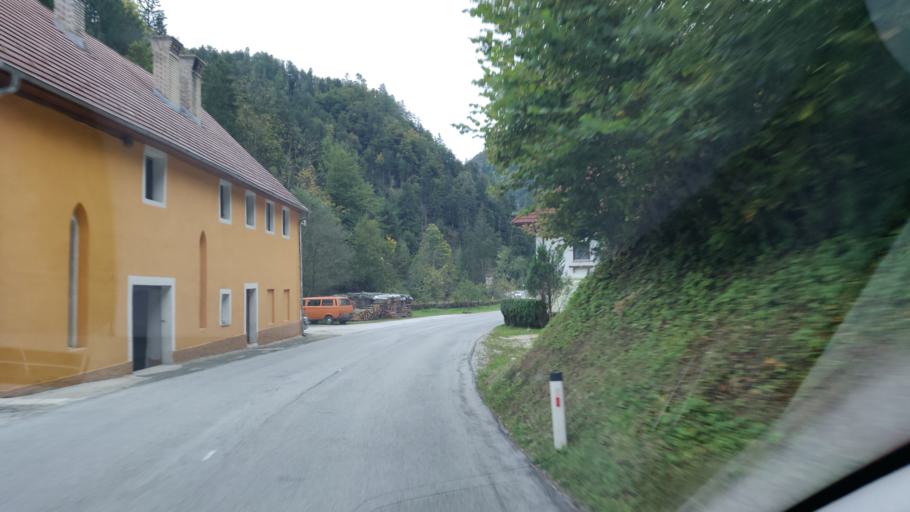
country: SI
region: Jezersko
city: Zgornje Jezersko
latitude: 46.3611
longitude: 14.4708
